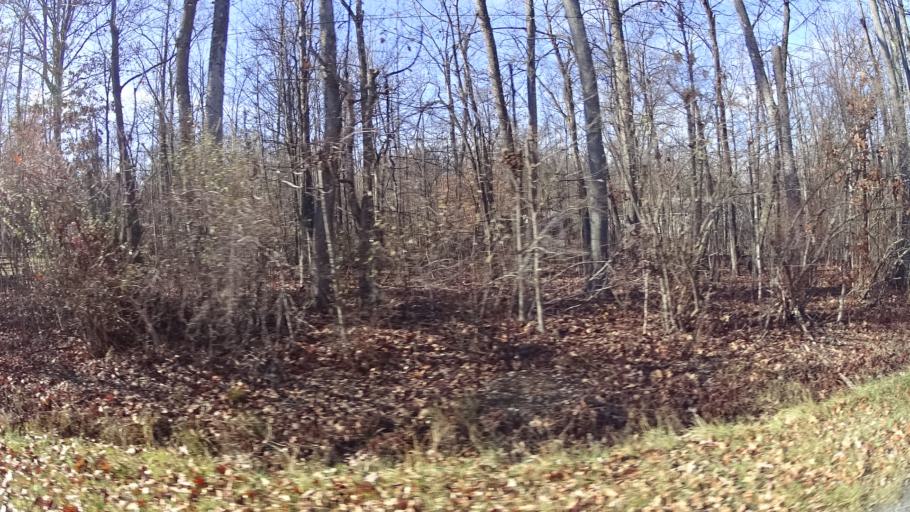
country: US
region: Ohio
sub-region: Lorain County
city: Wellington
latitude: 41.0650
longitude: -82.2017
